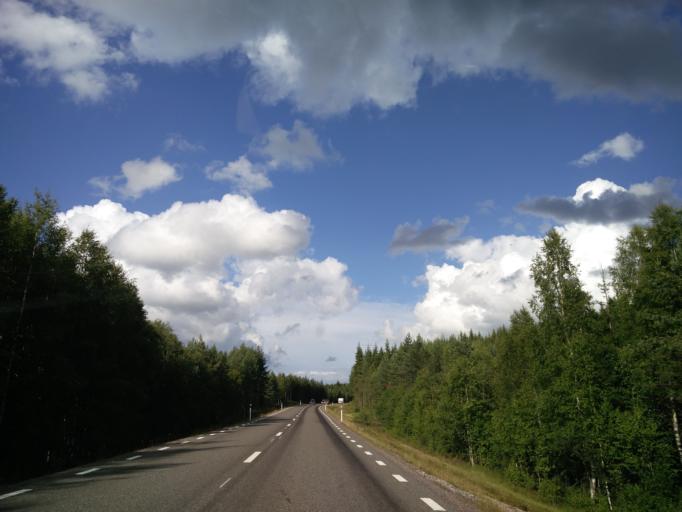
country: SE
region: Vaermland
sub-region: Torsby Kommun
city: Torsby
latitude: 60.3299
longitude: 13.1343
